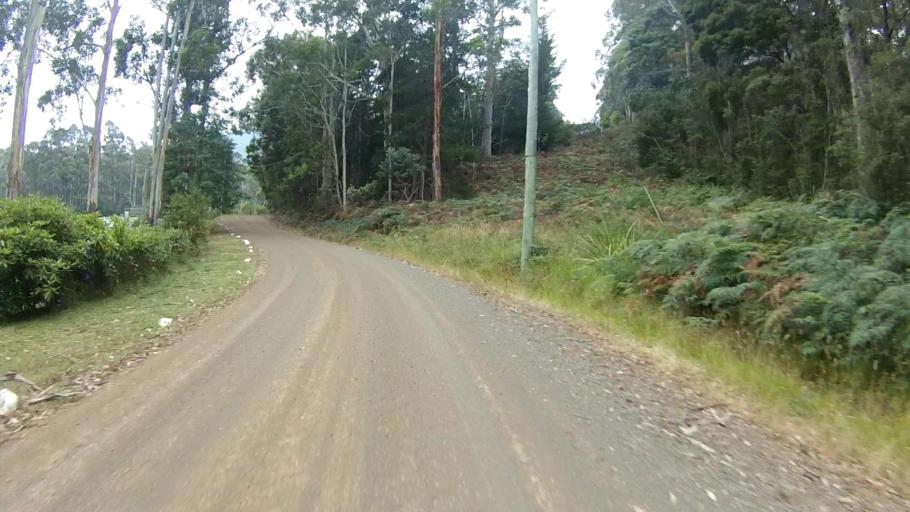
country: AU
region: Tasmania
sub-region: Huon Valley
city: Cygnet
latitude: -43.2327
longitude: 147.1587
